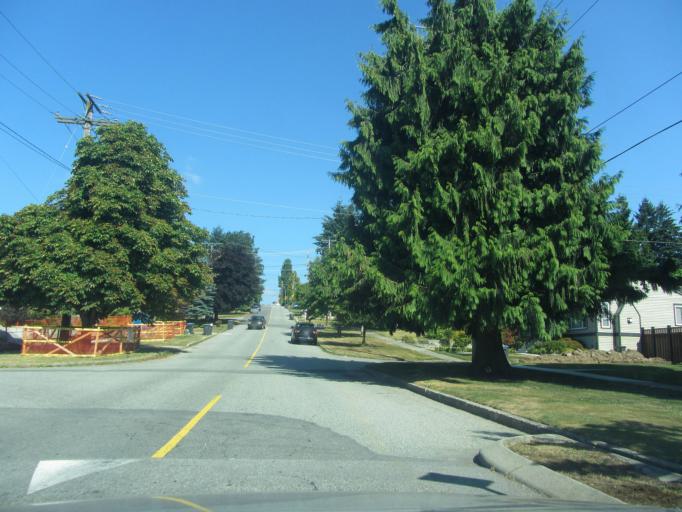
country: CA
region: British Columbia
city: New Westminster
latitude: 49.2210
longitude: -122.9198
